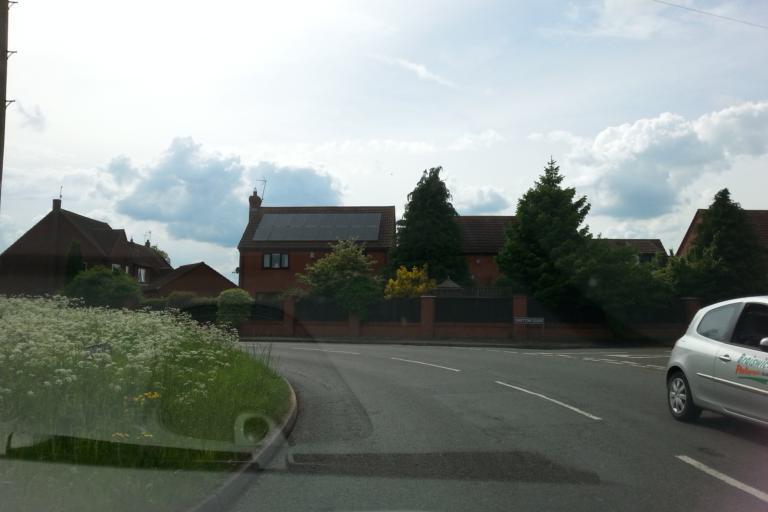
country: GB
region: England
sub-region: Lincolnshire
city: Long Bennington
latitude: 53.0313
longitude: -0.7437
